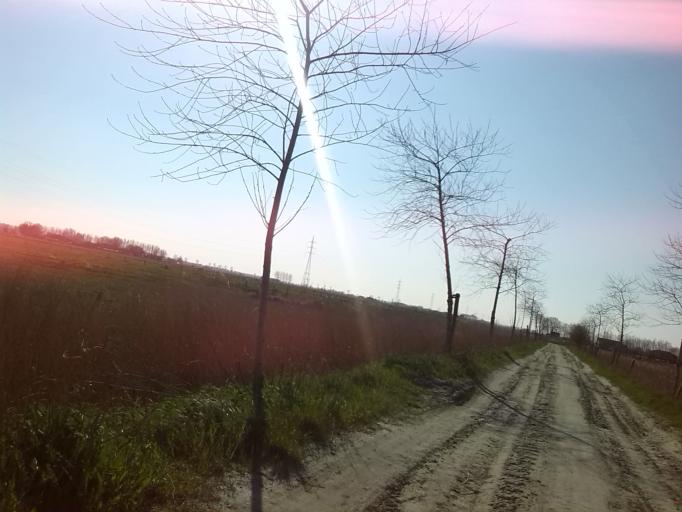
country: BE
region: Flanders
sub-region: Provincie West-Vlaanderen
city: Zuienkerke
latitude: 51.2226
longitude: 3.1397
